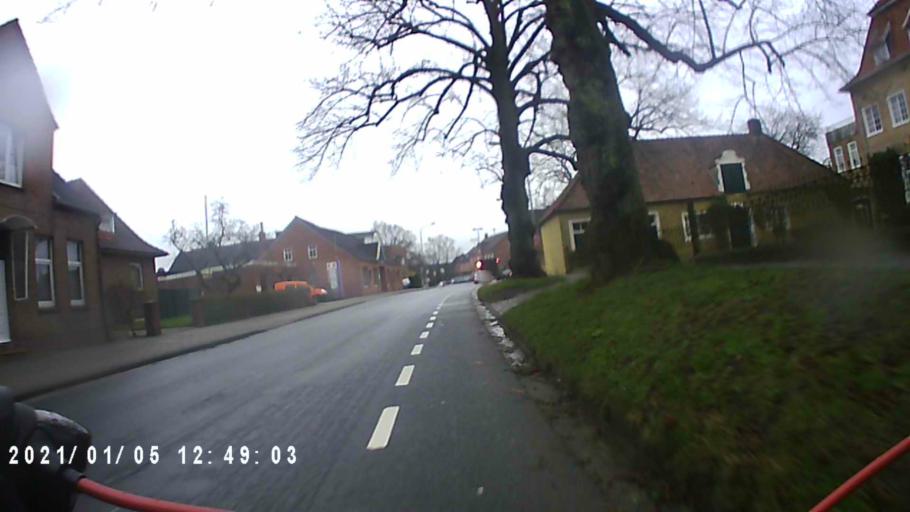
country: DE
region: Lower Saxony
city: Leer
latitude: 53.2378
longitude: 7.4974
